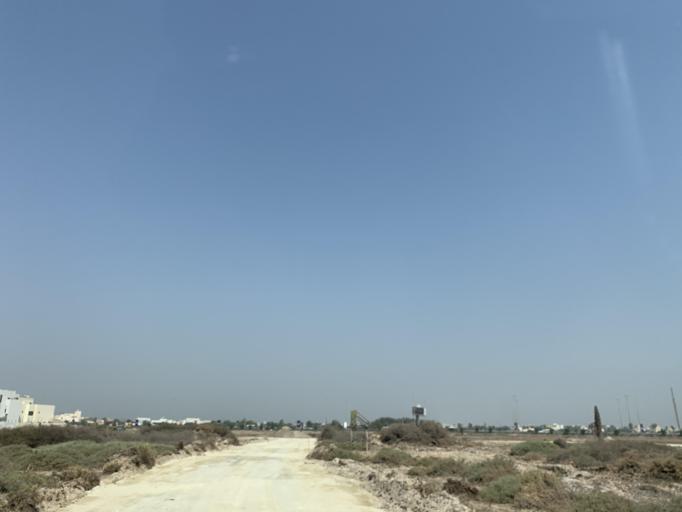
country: BH
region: Manama
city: Jidd Hafs
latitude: 26.2002
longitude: 50.5139
